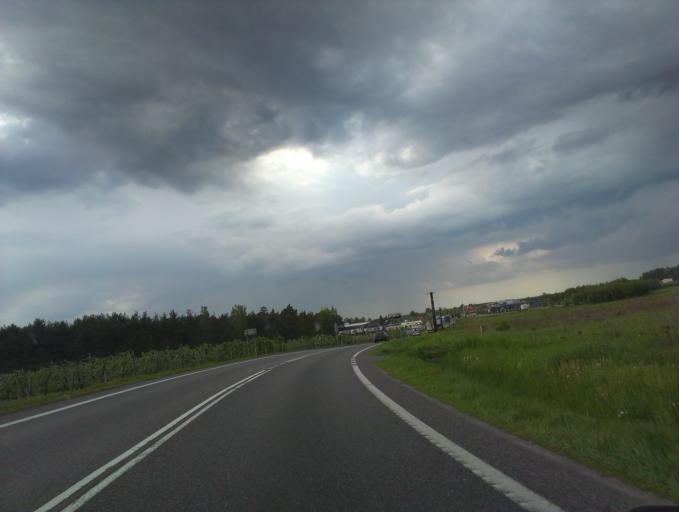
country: PL
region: Masovian Voivodeship
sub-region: Powiat grojecki
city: Pniewy
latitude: 51.9100
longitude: 20.7011
